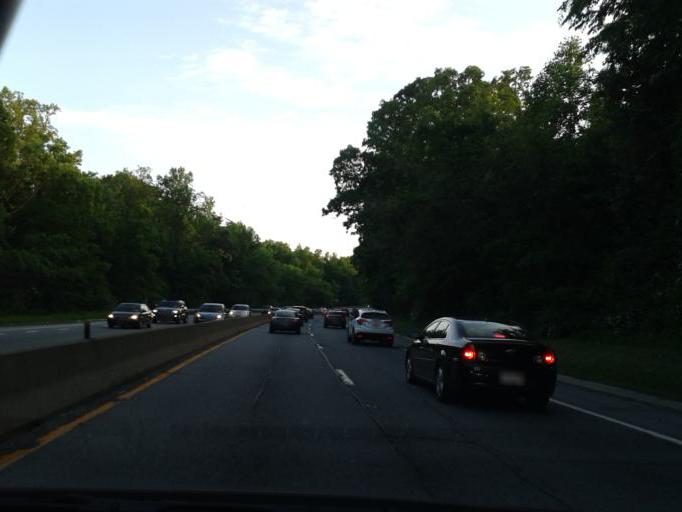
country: US
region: New York
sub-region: Westchester County
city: Scarsdale
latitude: 40.9733
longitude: -73.7655
